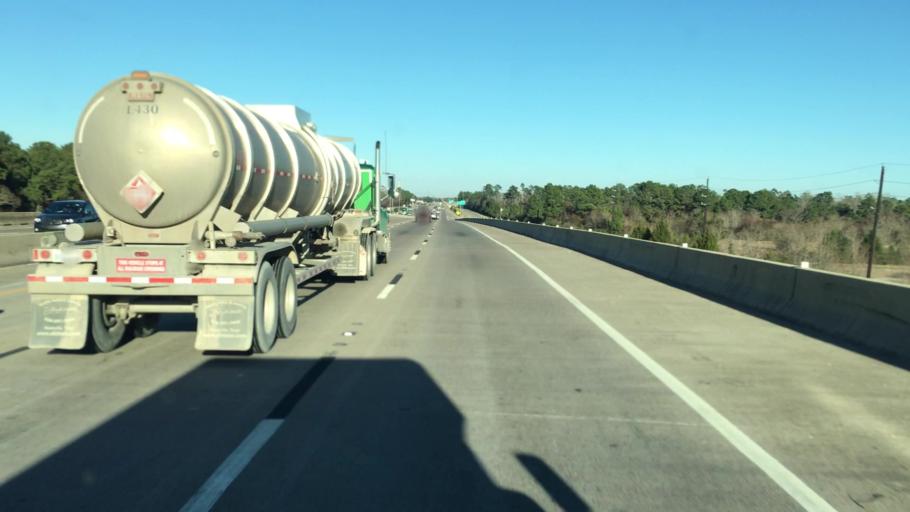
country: US
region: Texas
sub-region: Chambers County
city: Mont Belvieu
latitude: 29.8125
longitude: -94.9384
